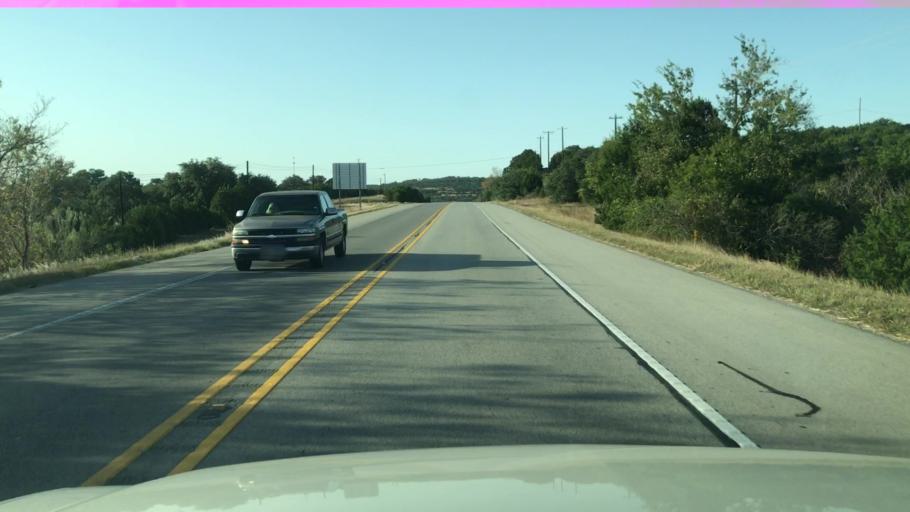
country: US
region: Texas
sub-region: Blanco County
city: Johnson City
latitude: 30.1923
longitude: -98.3768
